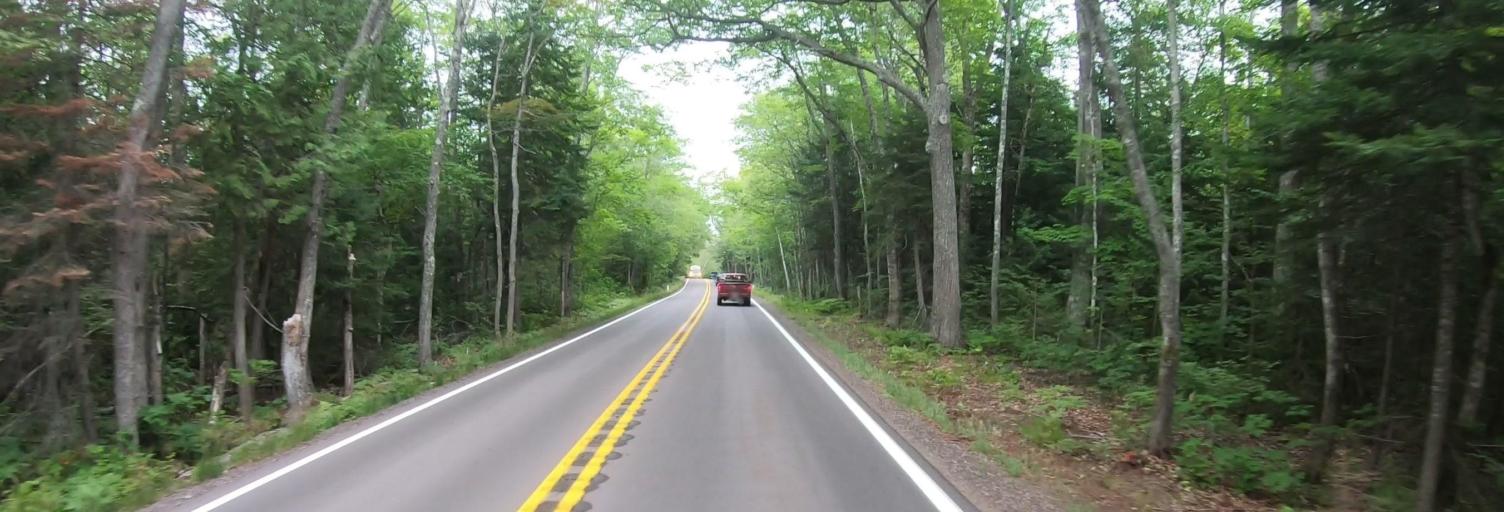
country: US
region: Michigan
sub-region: Keweenaw County
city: Eagle River
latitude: 47.4457
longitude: -87.9255
